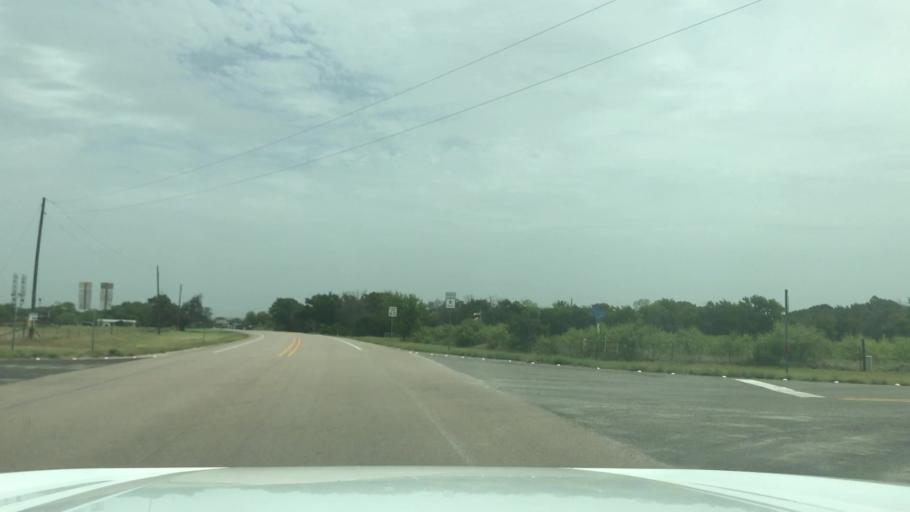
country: US
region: Texas
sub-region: Hamilton County
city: Hico
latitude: 31.9779
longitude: -97.8777
